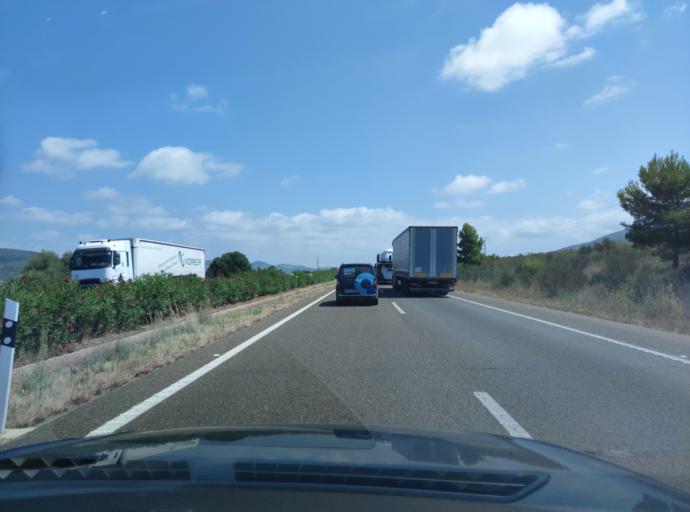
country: ES
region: Valencia
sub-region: Provincia de Castello
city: Alcala de Xivert
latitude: 40.3299
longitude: 0.2601
